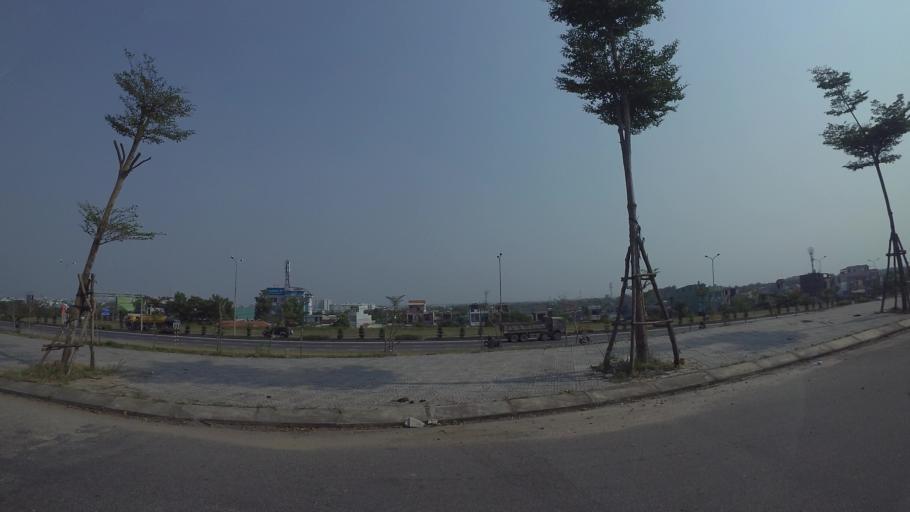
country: VN
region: Da Nang
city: Cam Le
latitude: 16.0142
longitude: 108.1898
